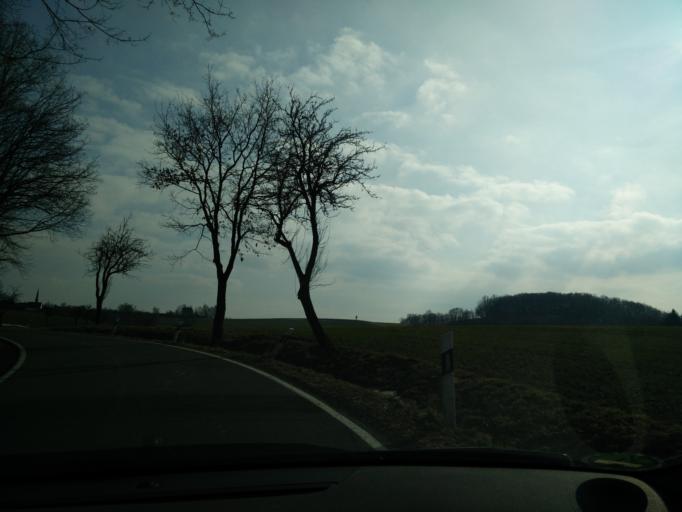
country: DE
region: Saxony
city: Colditz
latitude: 51.1098
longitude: 12.8164
